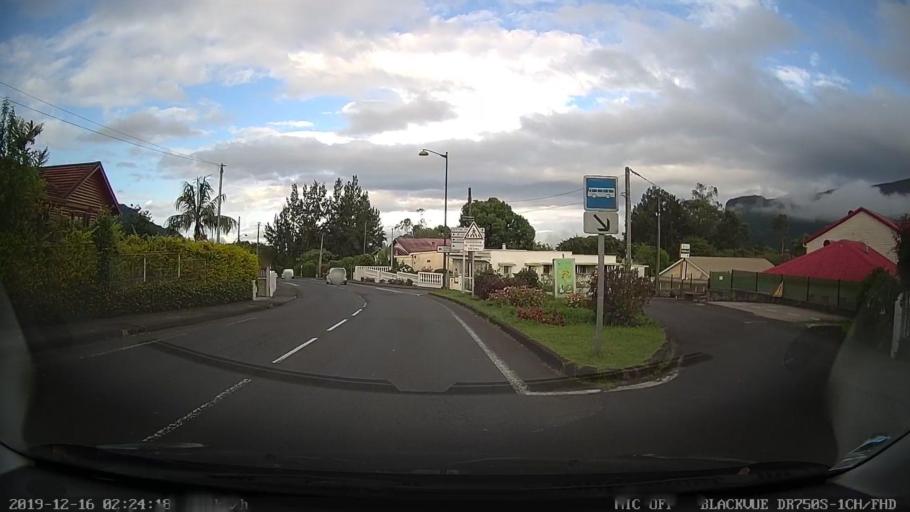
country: RE
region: Reunion
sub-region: Reunion
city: Saint-Benoit
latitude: -21.1384
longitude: 55.6237
